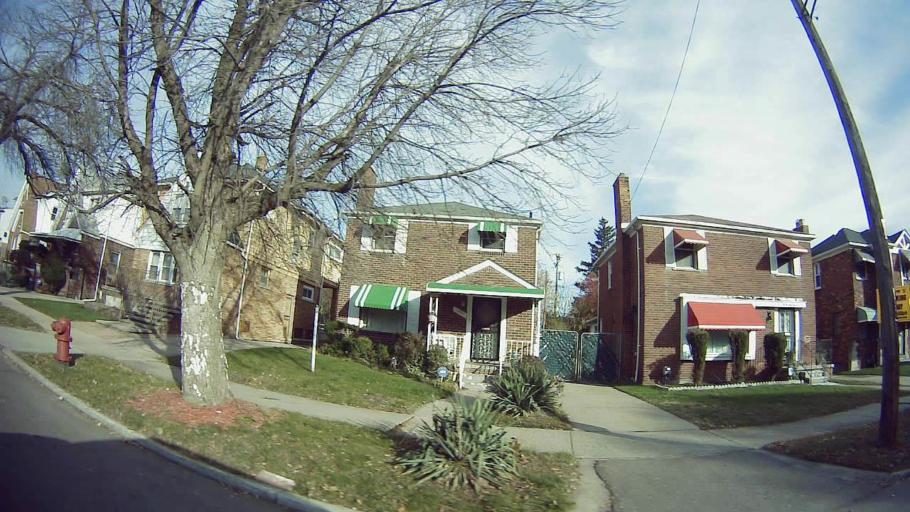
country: US
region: Michigan
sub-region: Oakland County
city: Oak Park
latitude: 42.4086
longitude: -83.1621
